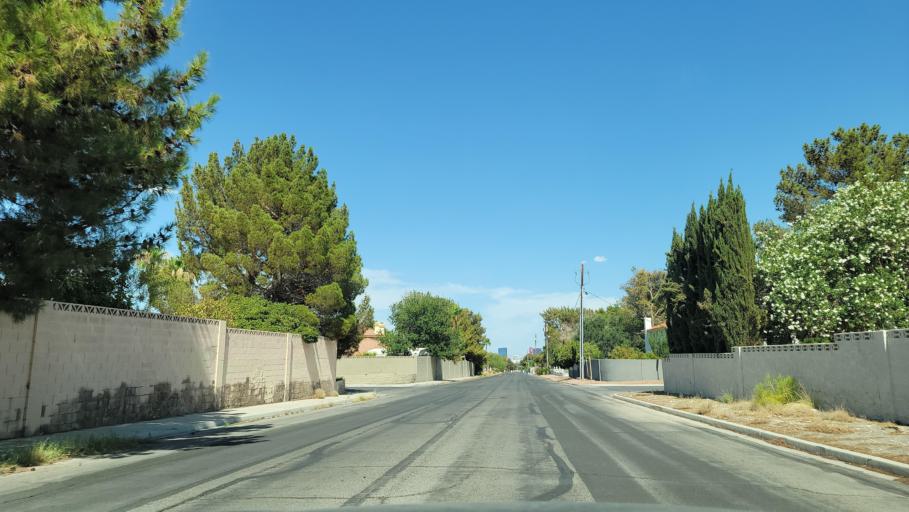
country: US
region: Nevada
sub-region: Clark County
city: Spring Valley
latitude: 36.1348
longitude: -115.2503
